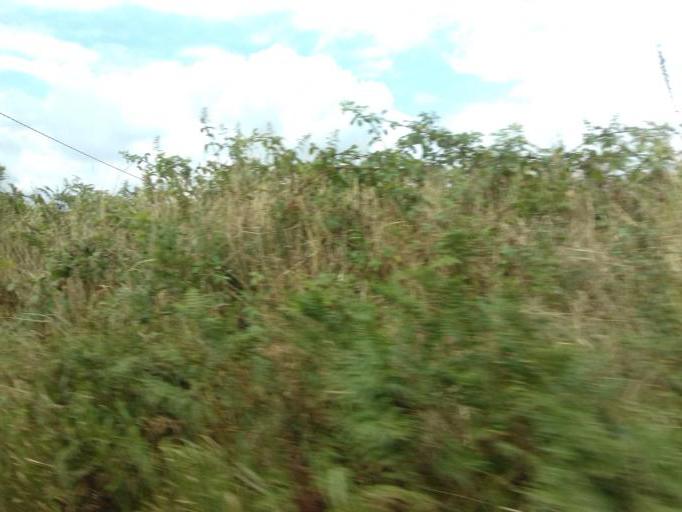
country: IE
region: Leinster
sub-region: Loch Garman
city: Ballinroad
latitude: 52.4754
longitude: -6.4092
